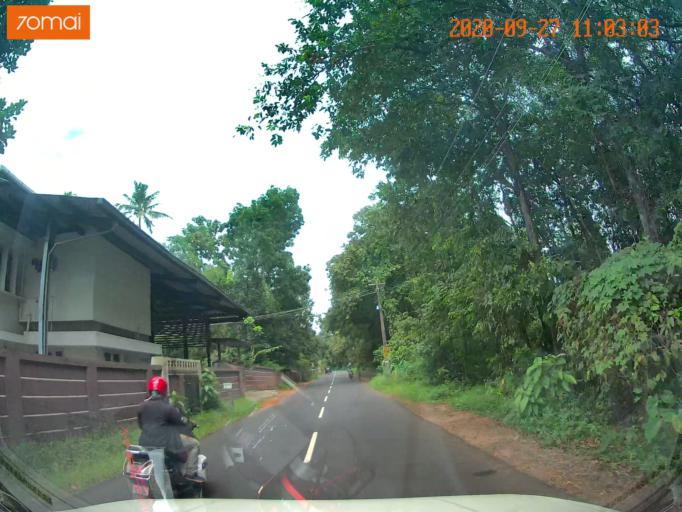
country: IN
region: Kerala
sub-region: Thrissur District
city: Irinjalakuda
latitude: 10.4203
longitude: 76.2603
